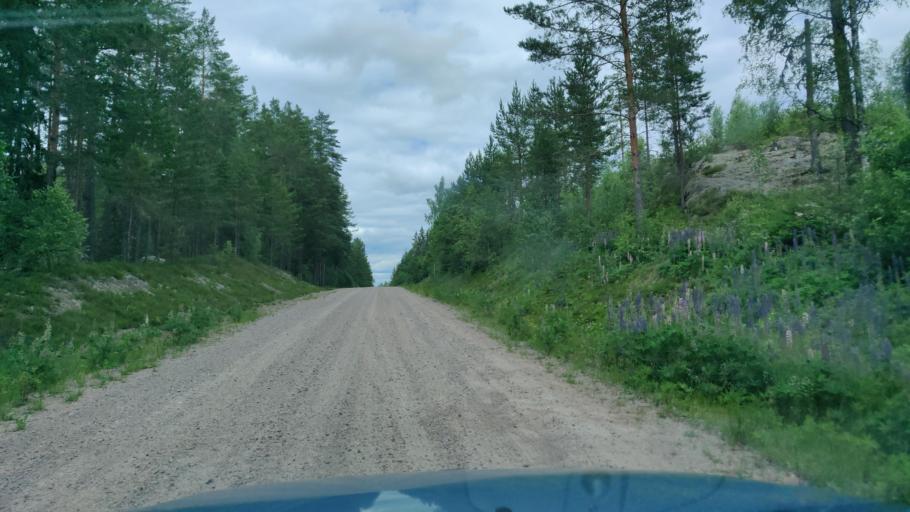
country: SE
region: Vaermland
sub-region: Hagfors Kommun
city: Hagfors
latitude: 60.0343
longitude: 13.7175
